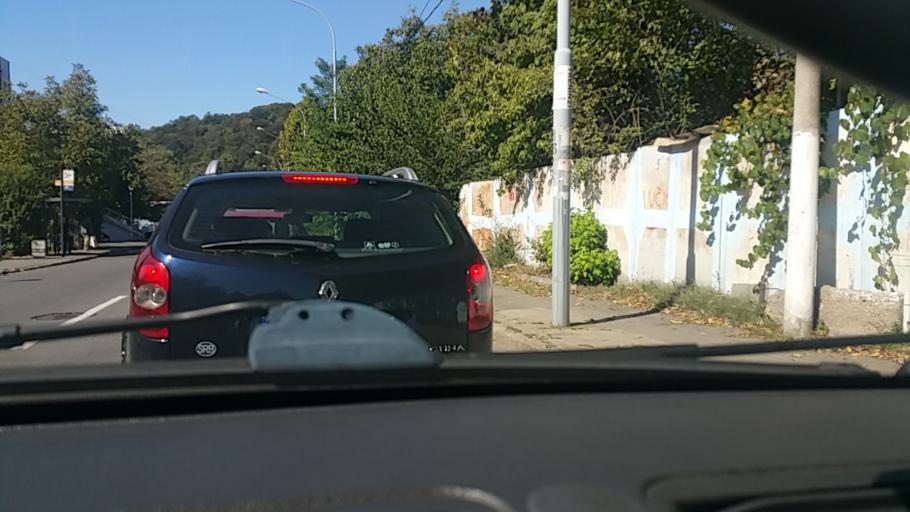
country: RS
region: Central Serbia
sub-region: Belgrade
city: Rakovica
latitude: 44.7508
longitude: 20.4502
